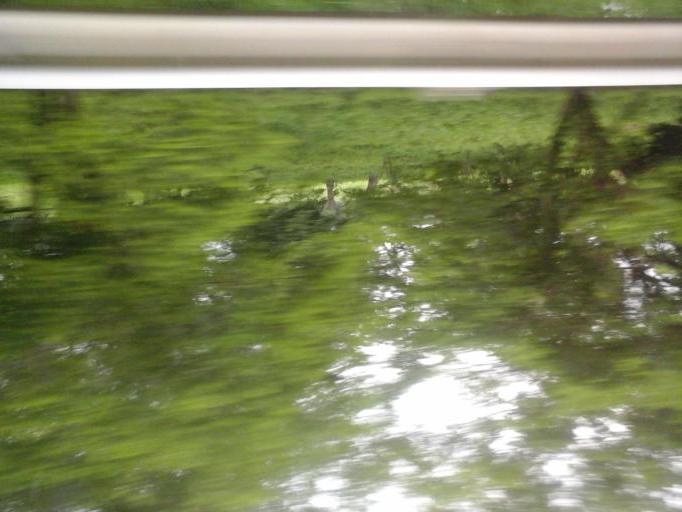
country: CO
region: Bolivar
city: San Pablo
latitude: 10.1370
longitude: -75.2721
